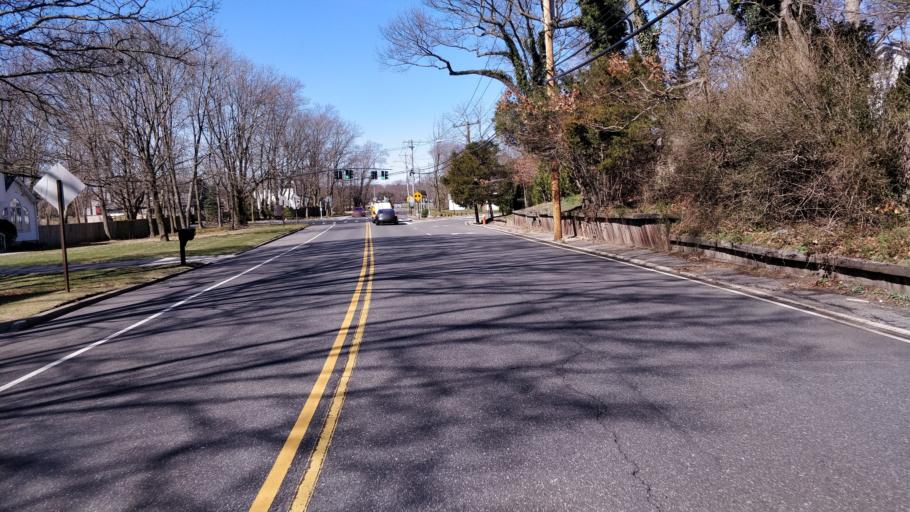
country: US
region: New York
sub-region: Suffolk County
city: Elwood
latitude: 40.8495
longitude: -73.3552
